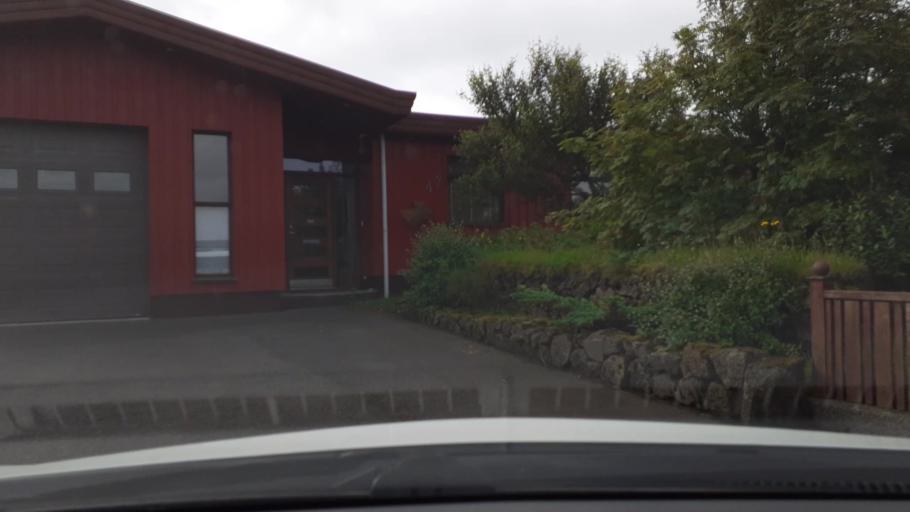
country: IS
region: South
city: THorlakshoefn
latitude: 63.8553
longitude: -21.3944
